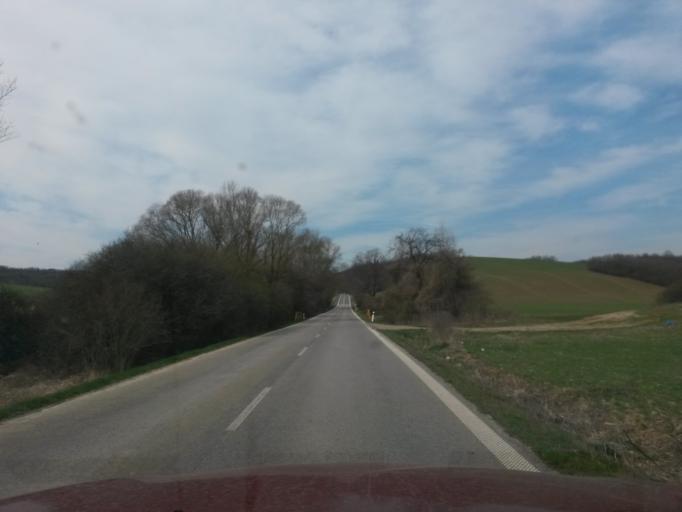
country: SK
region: Banskobystricky
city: Dudince
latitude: 48.1535
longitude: 18.9472
